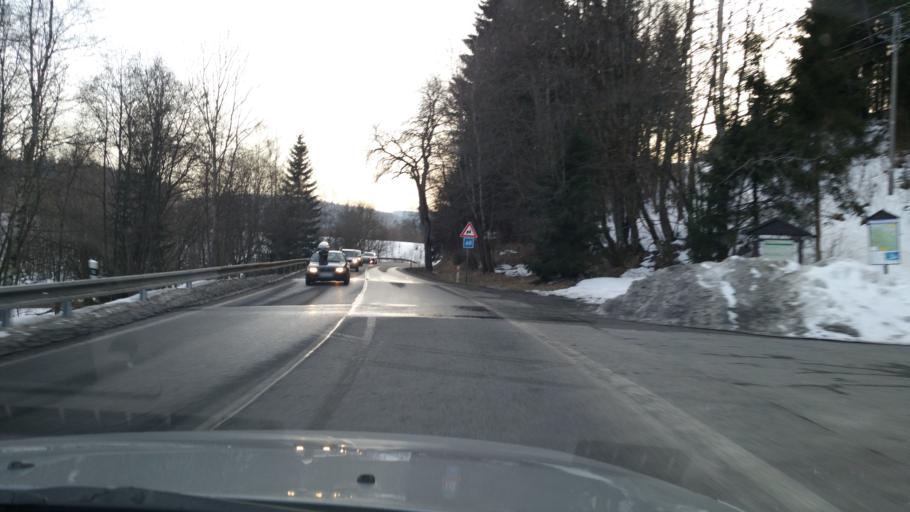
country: CZ
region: Plzensky
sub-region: Okres Klatovy
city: Zelezna Ruda
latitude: 49.1382
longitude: 13.2270
